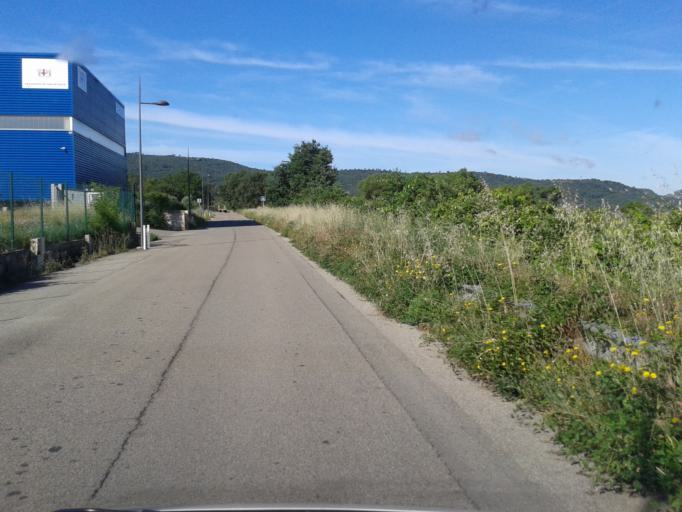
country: FR
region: Provence-Alpes-Cote d'Azur
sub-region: Departement du Vaucluse
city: Beaumont-de-Pertuis
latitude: 43.6955
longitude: 5.7303
